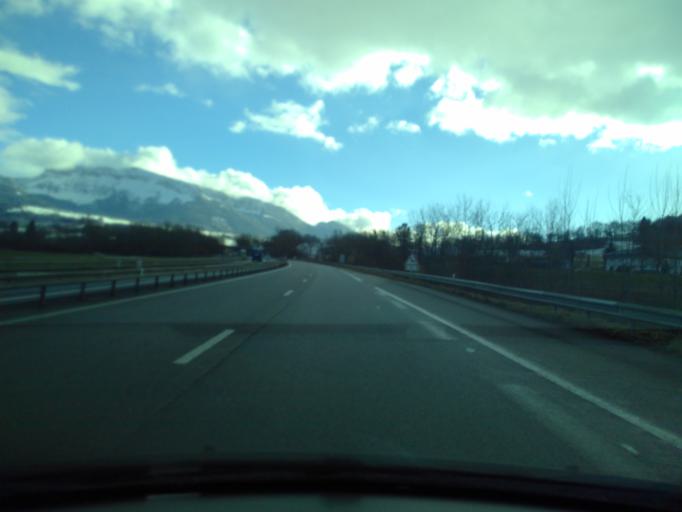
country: FR
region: Rhone-Alpes
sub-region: Departement de la Haute-Savoie
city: Etaux
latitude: 46.0685
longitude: 6.2892
